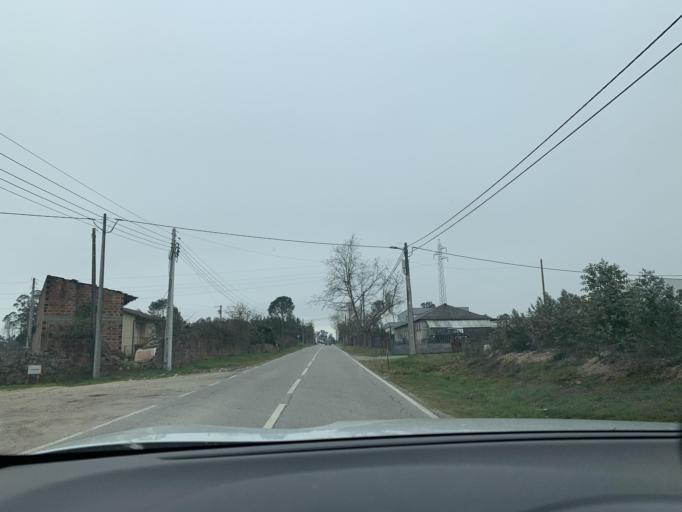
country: PT
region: Viseu
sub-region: Concelho de Tondela
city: Tondela
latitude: 40.5334
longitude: -8.0538
